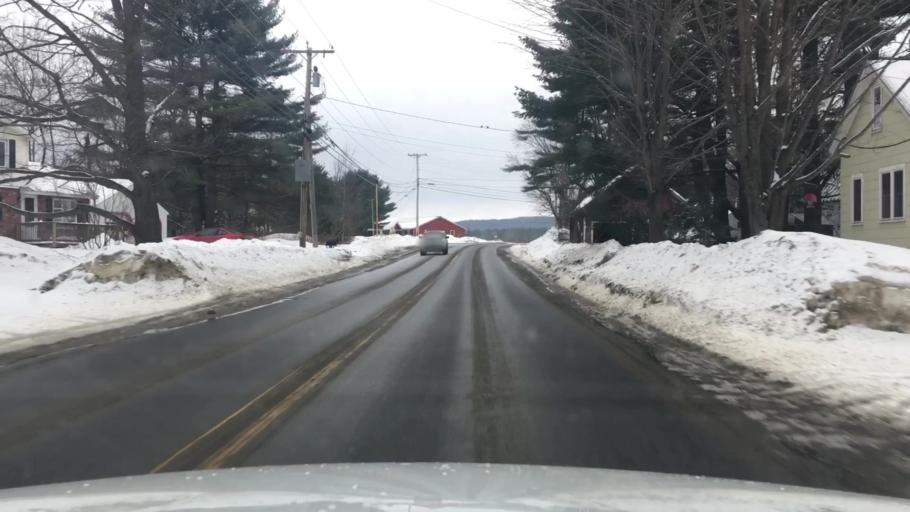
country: US
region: Maine
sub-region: Somerset County
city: Norridgewock
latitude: 44.7079
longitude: -69.7913
